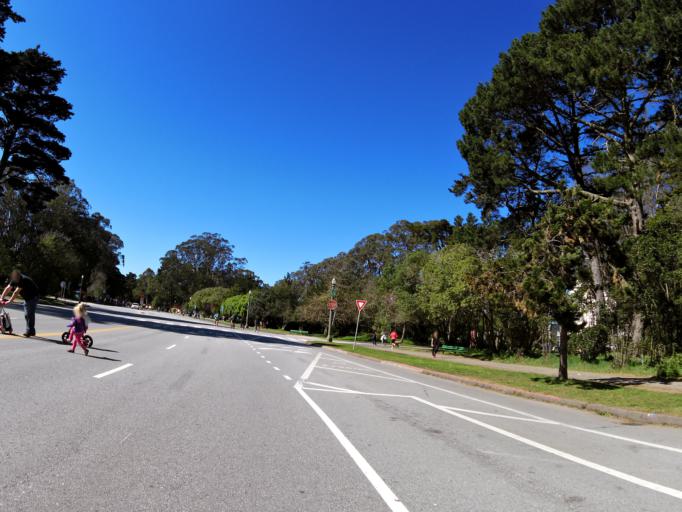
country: US
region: California
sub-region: San Francisco County
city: San Francisco
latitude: 37.7726
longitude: -122.4652
